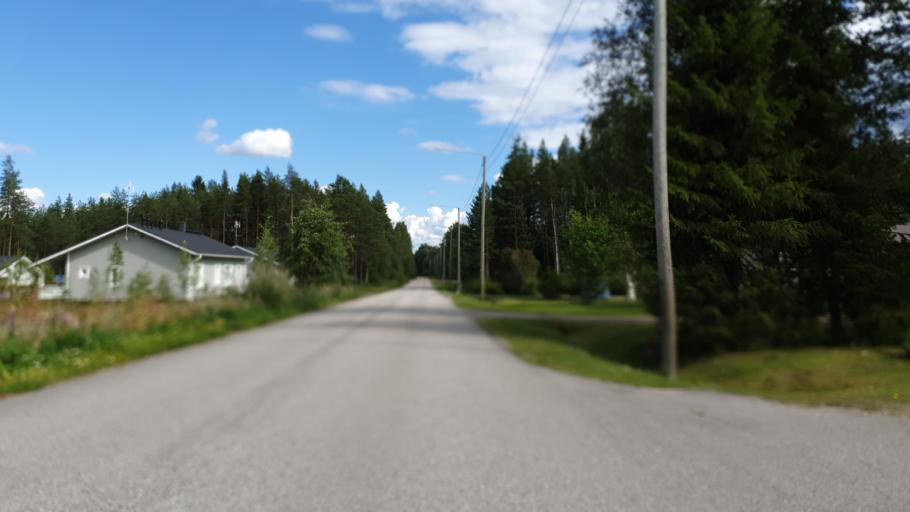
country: FI
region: Kainuu
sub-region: Kehys-Kainuu
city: Kuhmo
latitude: 64.1195
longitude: 29.5563
